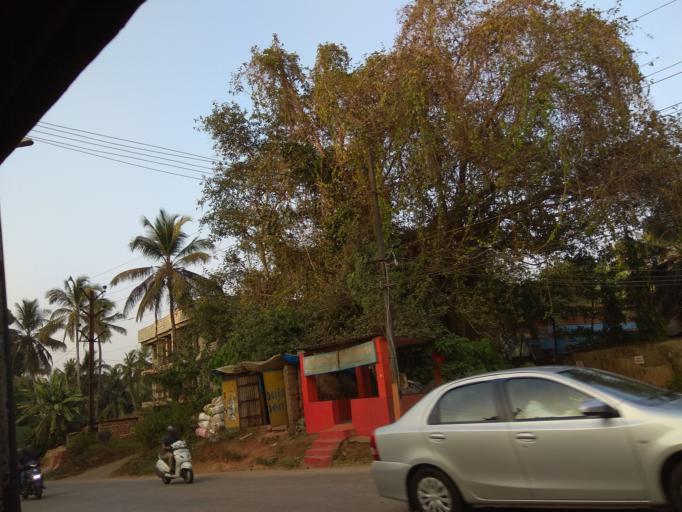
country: IN
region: Karnataka
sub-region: Dakshina Kannada
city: Mangalore
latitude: 12.9298
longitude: 74.8588
